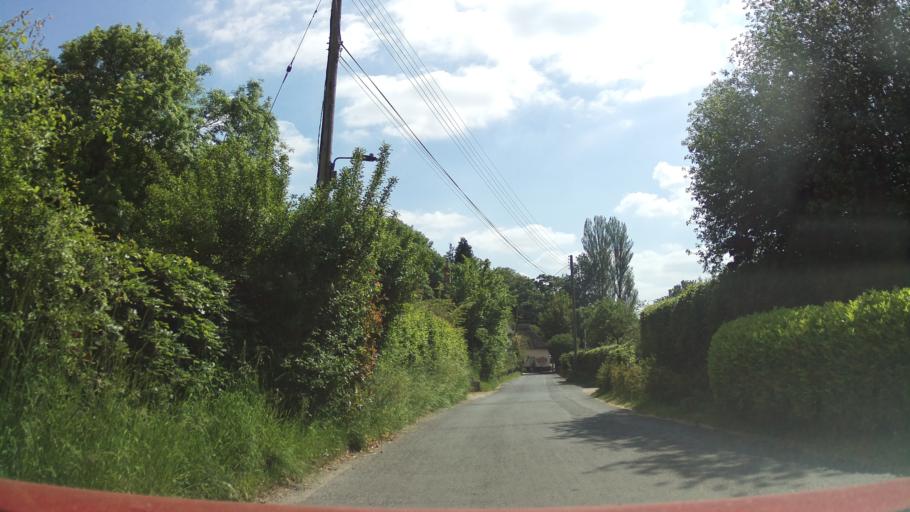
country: GB
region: England
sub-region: Wiltshire
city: Rushall
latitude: 51.2737
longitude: -1.8002
